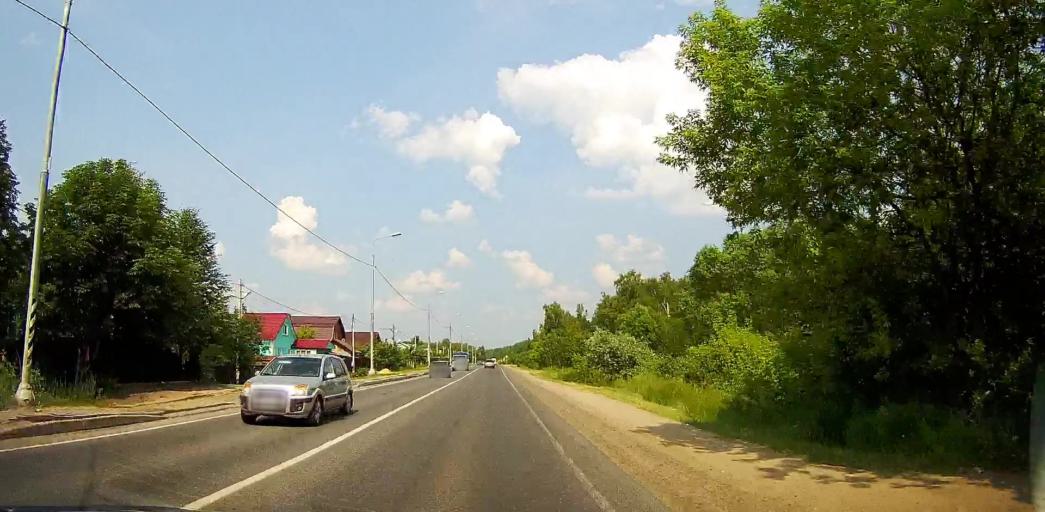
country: RU
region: Moskovskaya
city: Stupino
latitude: 54.9146
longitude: 38.1011
